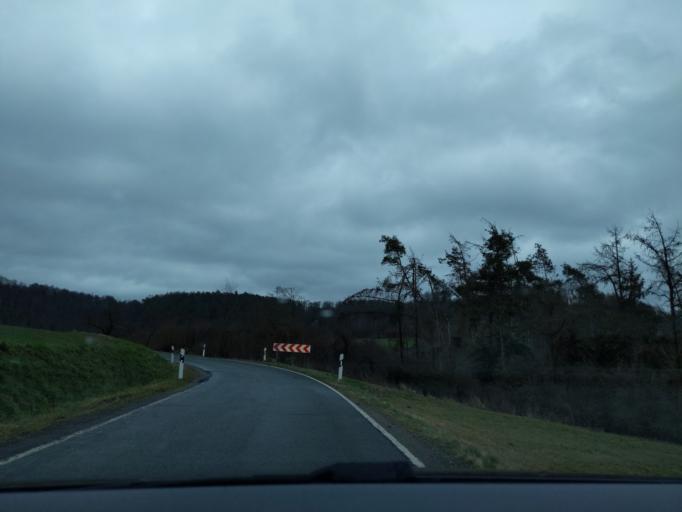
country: DE
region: Hesse
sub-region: Regierungsbezirk Kassel
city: Bad Arolsen
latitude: 51.3215
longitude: 9.0173
